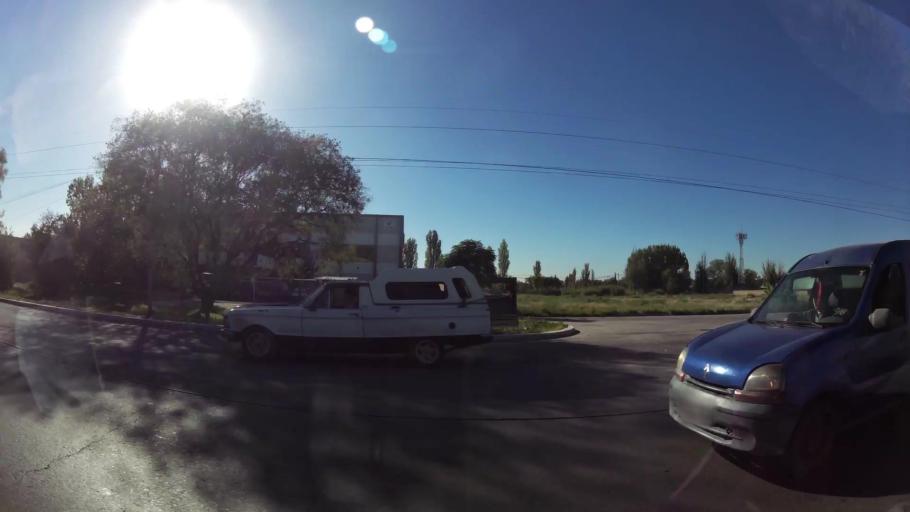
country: AR
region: Mendoza
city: Las Heras
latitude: -32.8507
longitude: -68.8048
